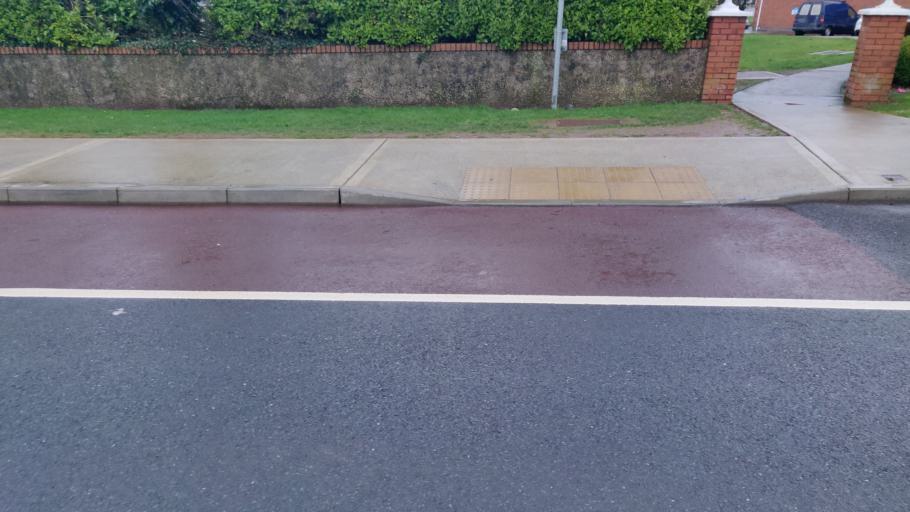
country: IE
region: Munster
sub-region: County Cork
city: Carrigaline
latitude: 51.8644
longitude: -8.4134
